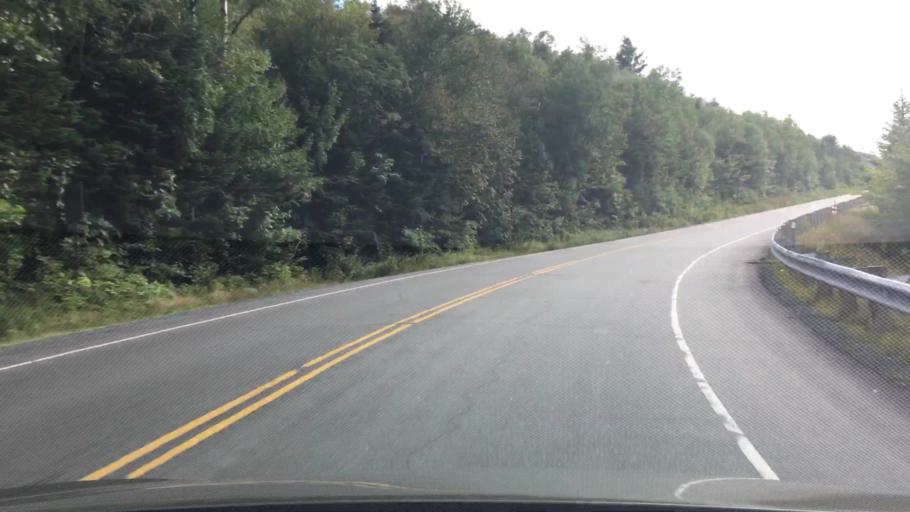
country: US
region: New Hampshire
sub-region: Grafton County
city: Woodstock
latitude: 44.0345
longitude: -71.4960
